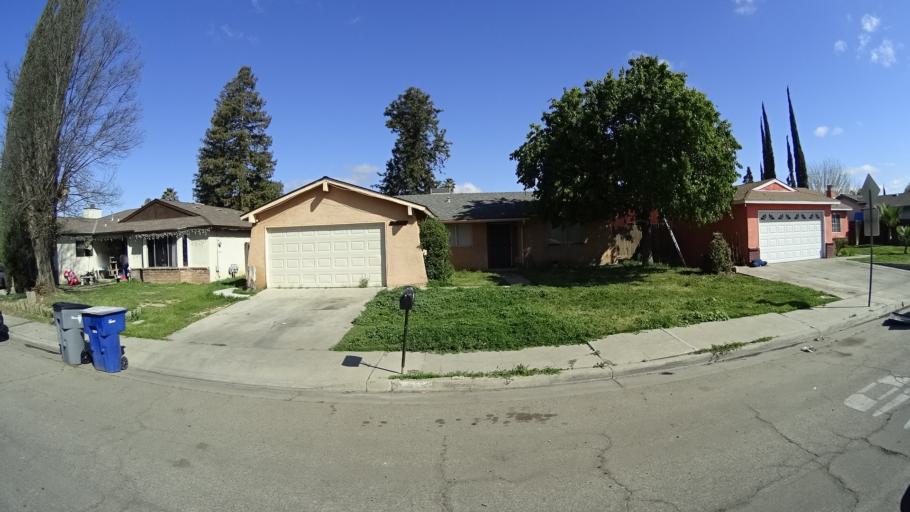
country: US
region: California
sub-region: Fresno County
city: West Park
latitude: 36.7968
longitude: -119.8840
